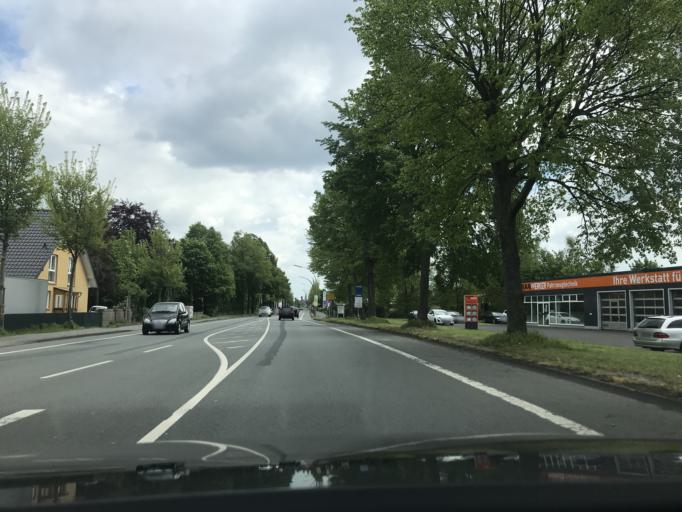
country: DE
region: North Rhine-Westphalia
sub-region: Regierungsbezirk Detmold
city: Rheda-Wiedenbruck
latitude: 51.8615
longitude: 8.2753
